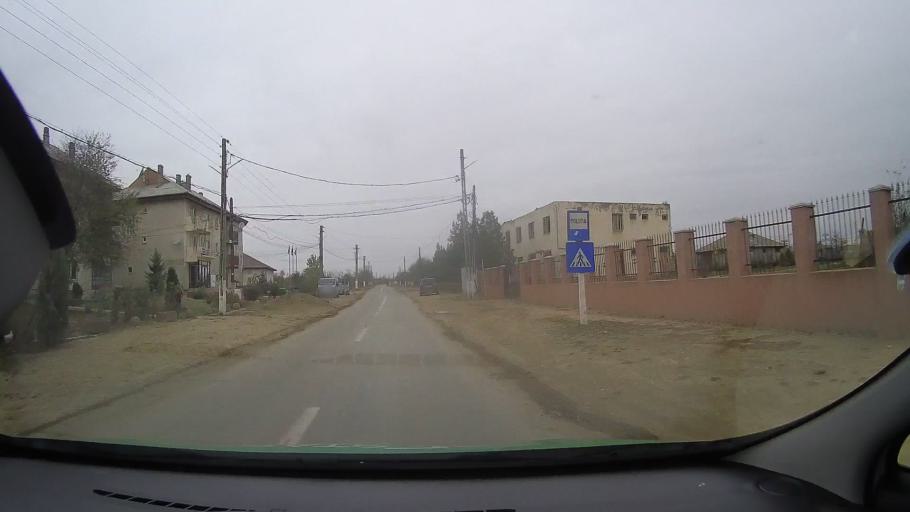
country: RO
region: Constanta
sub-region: Comuna Vulturu
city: Vulturu
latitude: 44.6484
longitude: 28.2692
